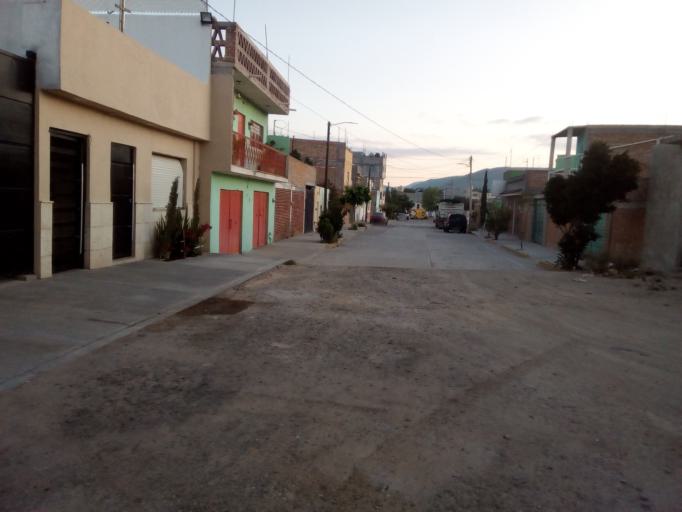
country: MX
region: Guerrero
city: San Luis de la Paz
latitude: 21.2908
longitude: -100.5200
